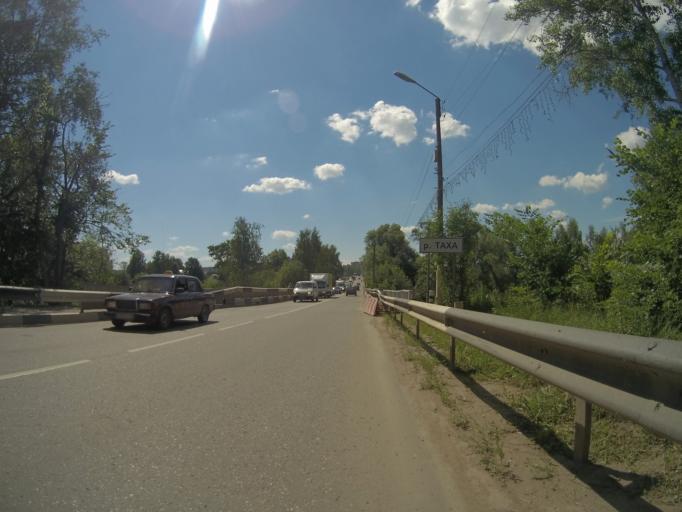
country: RU
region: Ivanovo
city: Privolzhsk
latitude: 57.3774
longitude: 41.2795
